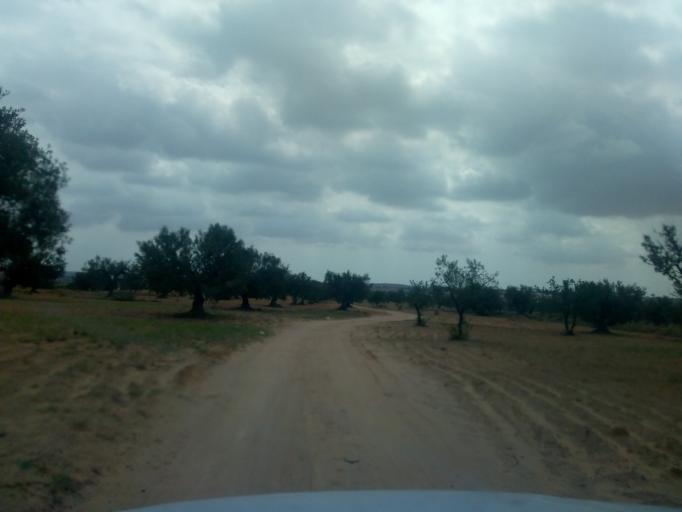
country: TN
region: Safaqis
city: Sfax
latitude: 34.7476
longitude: 10.4883
